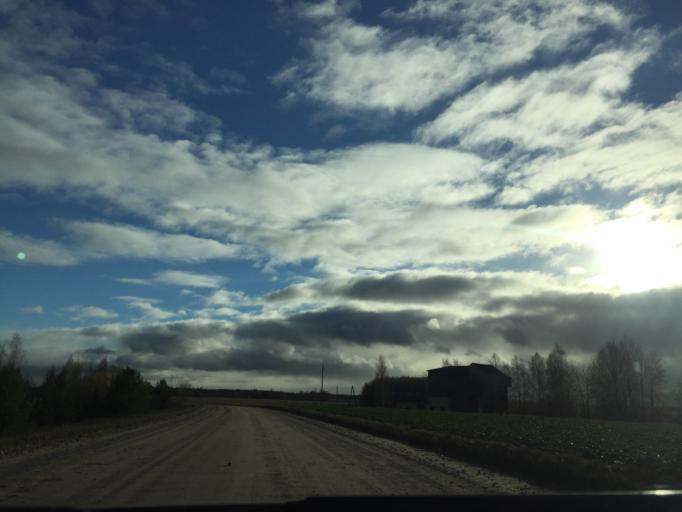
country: LV
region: Kandava
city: Kandava
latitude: 56.9668
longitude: 22.9367
